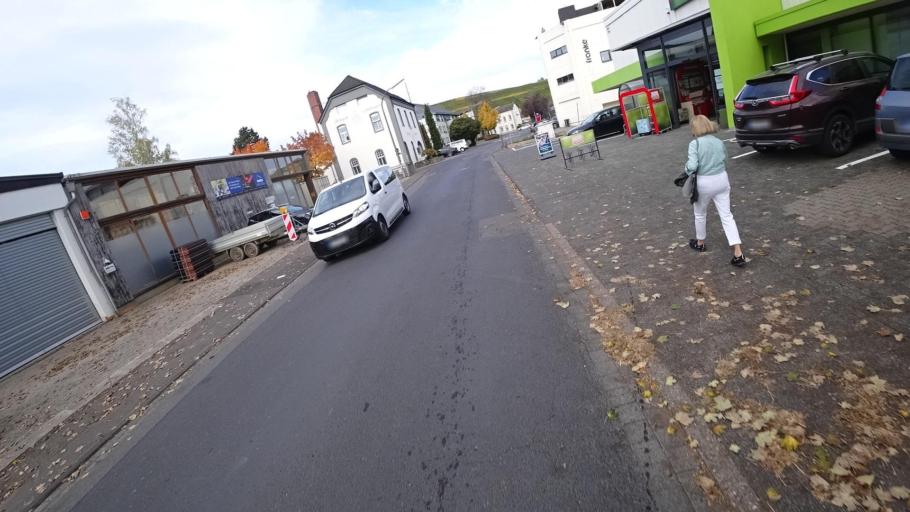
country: DE
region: Rheinland-Pfalz
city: Bad Neuenahr-Ahrweiler
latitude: 50.5441
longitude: 7.1085
